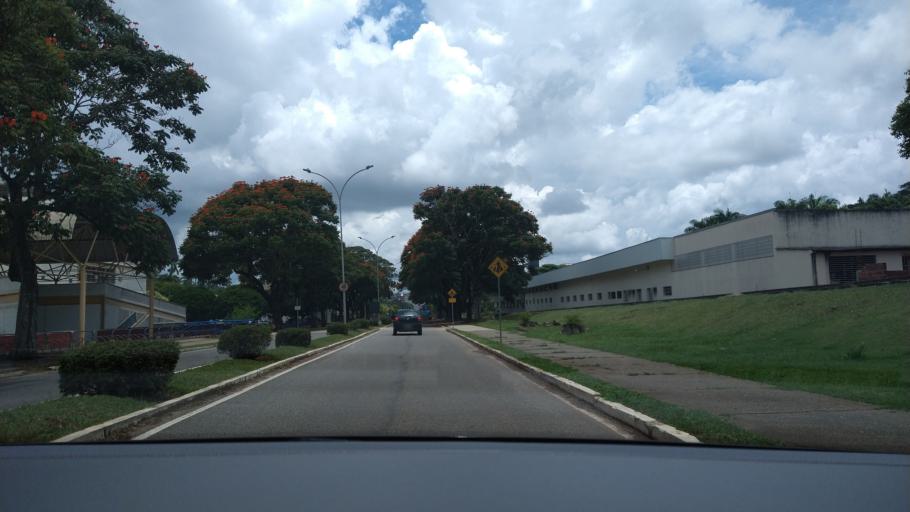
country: BR
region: Minas Gerais
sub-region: Vicosa
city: Vicosa
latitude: -20.7637
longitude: -42.8657
